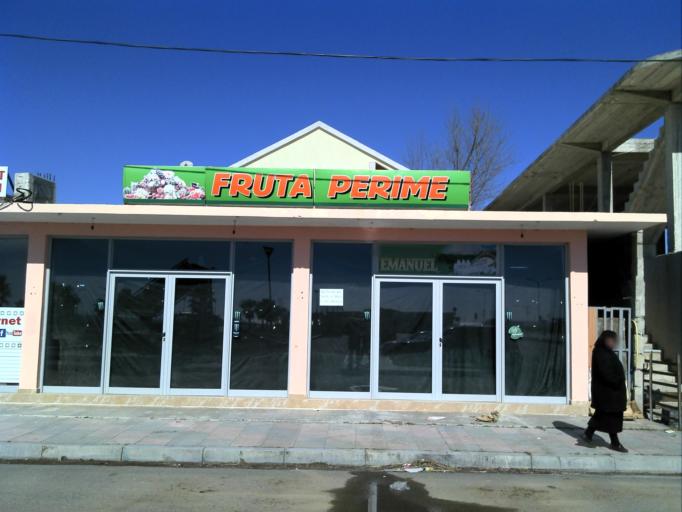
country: AL
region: Shkoder
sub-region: Rrethi i Shkodres
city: Velipoje
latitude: 41.8638
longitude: 19.4255
